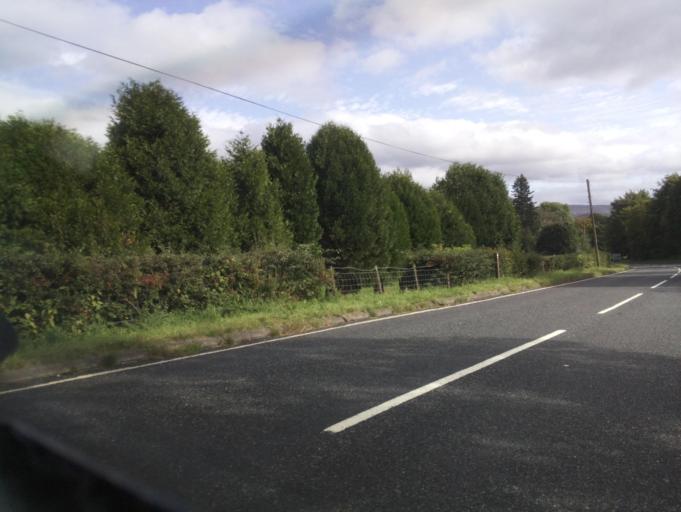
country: GB
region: Scotland
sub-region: Dumfries and Galloway
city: Moffat
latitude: 55.3383
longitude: -3.4562
